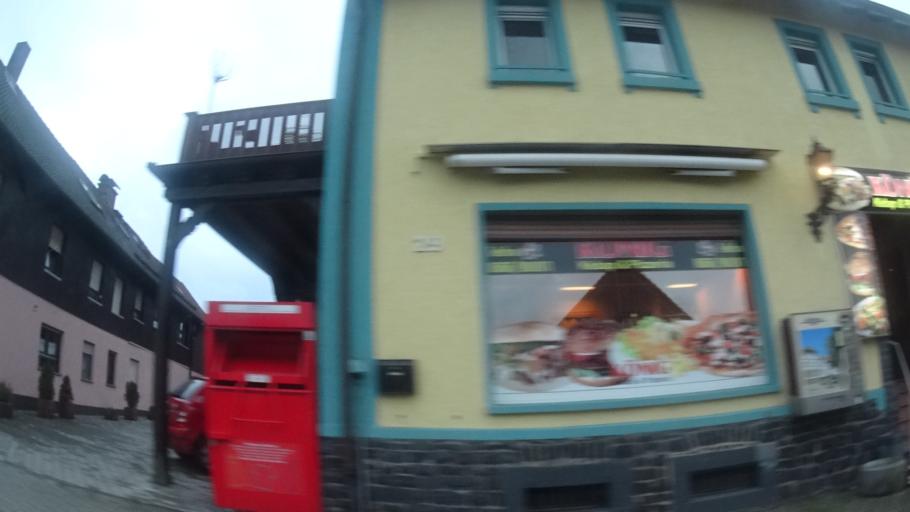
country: DE
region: Hesse
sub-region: Regierungsbezirk Giessen
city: Freiensteinau
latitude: 50.4241
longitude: 9.4035
